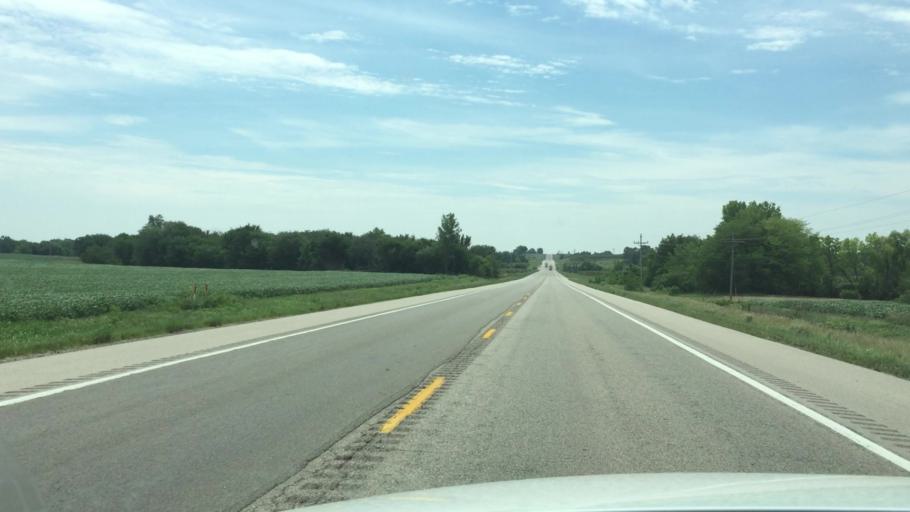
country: US
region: Kansas
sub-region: Nemaha County
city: Sabetha
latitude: 39.8068
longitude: -95.7294
